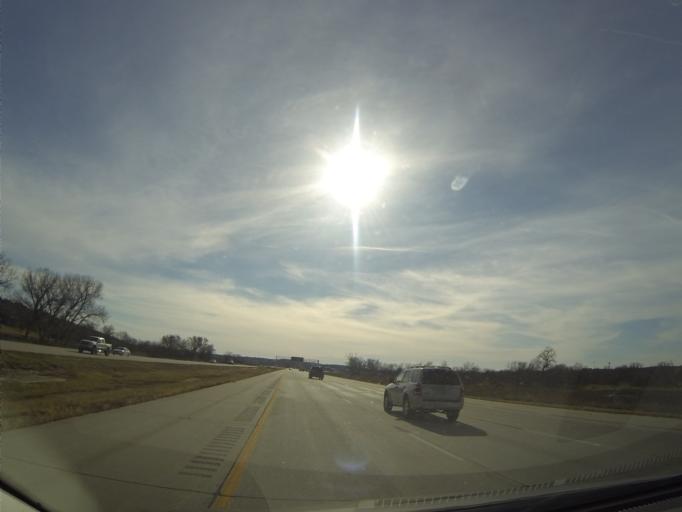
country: US
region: Nebraska
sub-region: Saunders County
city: Ashland
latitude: 41.0433
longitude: -96.2941
